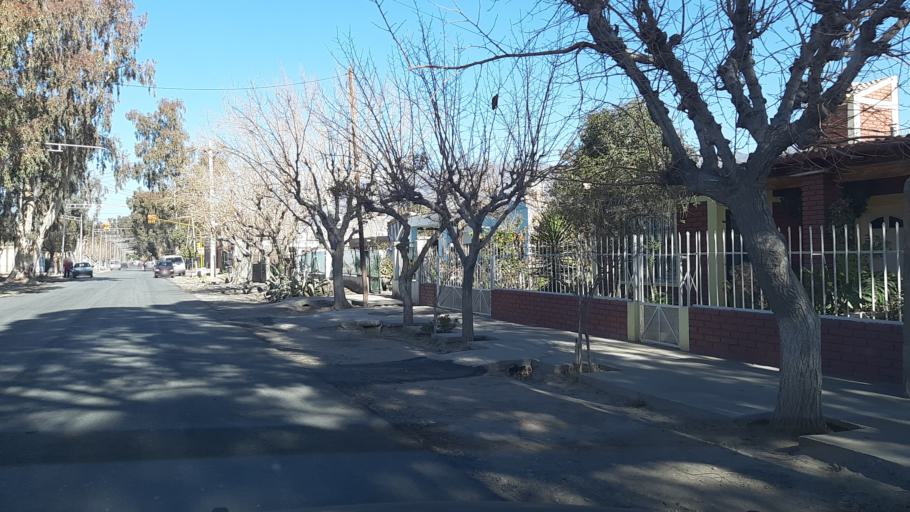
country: AR
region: San Juan
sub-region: Departamento de Zonda
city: Zonda
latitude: -31.5476
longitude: -68.7291
